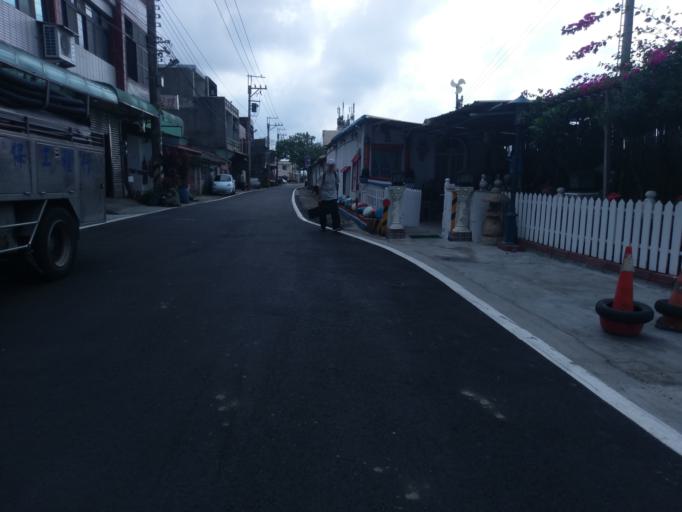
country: TW
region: Taiwan
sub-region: Miaoli
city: Miaoli
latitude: 24.6456
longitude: 120.8039
